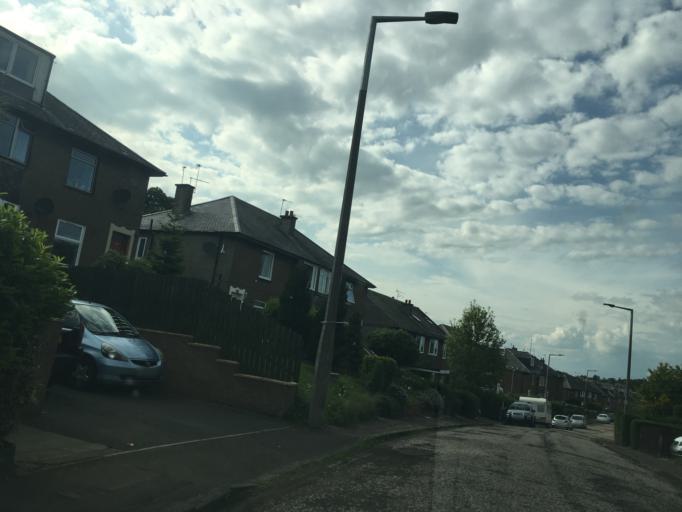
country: GB
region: Scotland
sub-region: Edinburgh
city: Colinton
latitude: 55.9062
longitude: -3.2332
